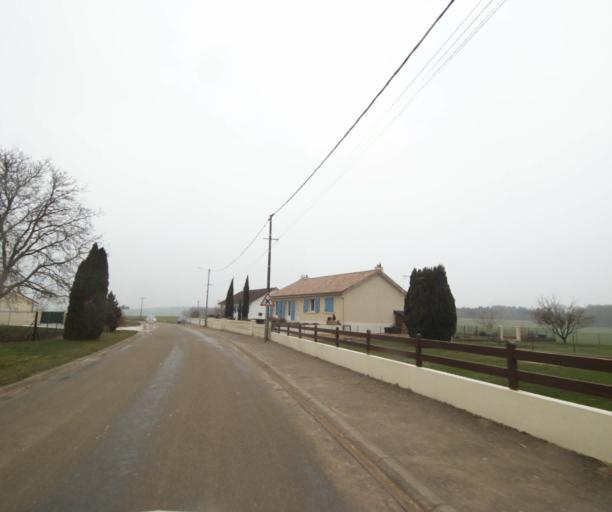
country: FR
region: Champagne-Ardenne
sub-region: Departement de la Haute-Marne
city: Bienville
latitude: 48.5296
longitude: 5.0446
